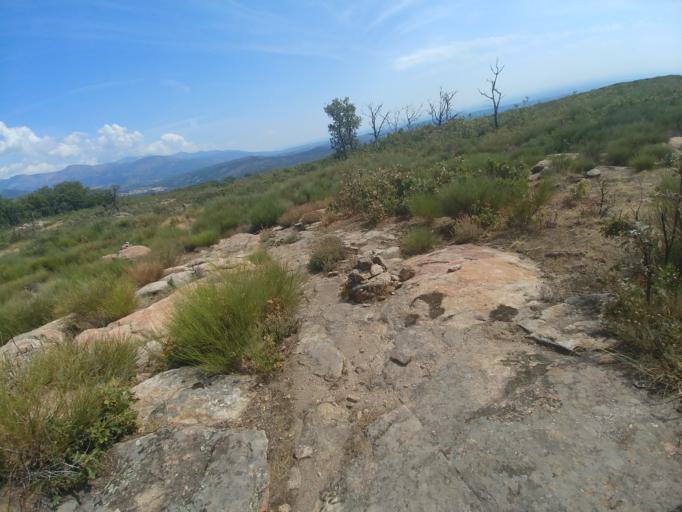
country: ES
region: Extremadura
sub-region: Provincia de Caceres
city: Garganta la Olla
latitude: 40.1038
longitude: -5.7591
